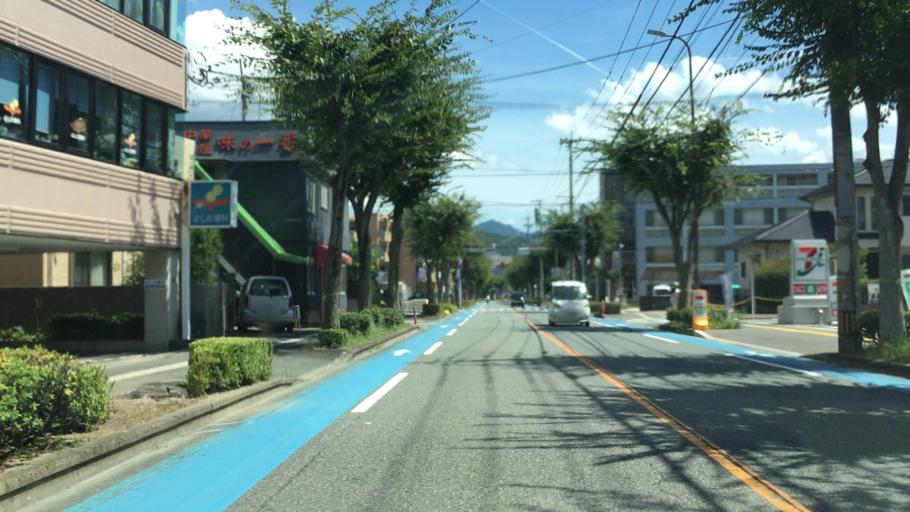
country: JP
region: Fukuoka
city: Onojo
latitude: 33.5414
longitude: 130.4759
